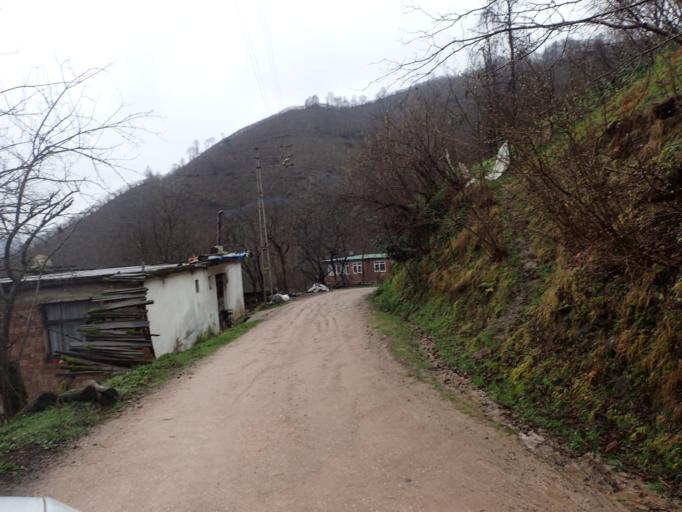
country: TR
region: Ordu
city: Camas
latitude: 40.9126
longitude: 37.5675
